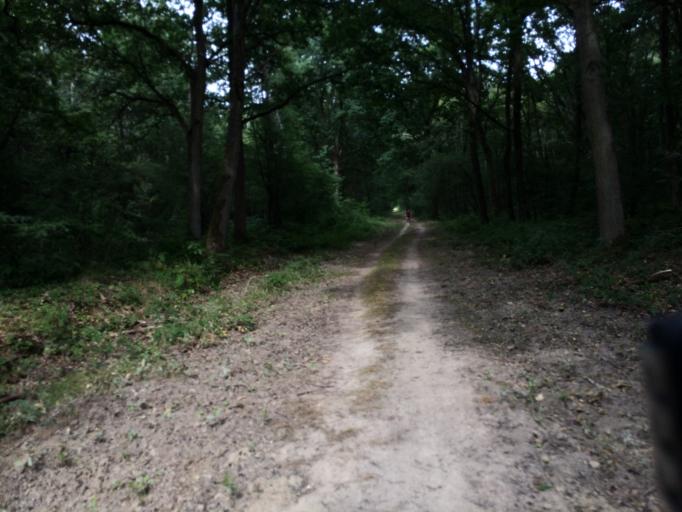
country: FR
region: Ile-de-France
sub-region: Departement de l'Essonne
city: Soisy-sur-Seine
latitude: 48.6710
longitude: 2.4569
